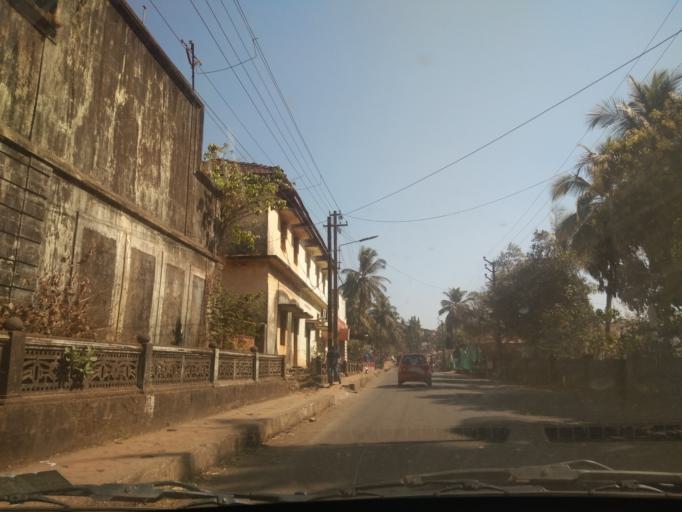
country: IN
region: Goa
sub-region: North Goa
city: Sanquelim
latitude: 15.5615
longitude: 74.0126
